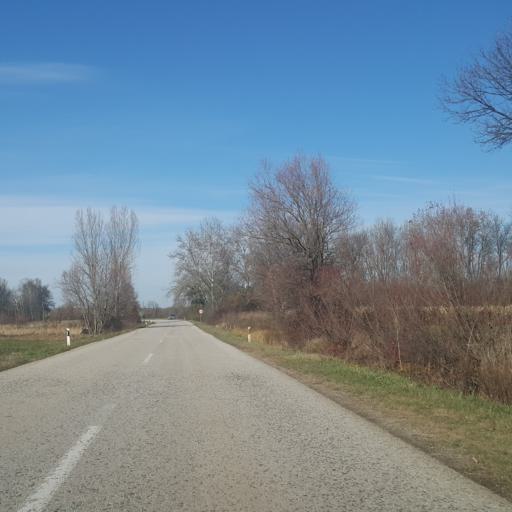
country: RS
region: Central Serbia
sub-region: Sumadijski Okrug
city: Topola
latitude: 44.2511
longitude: 20.8295
